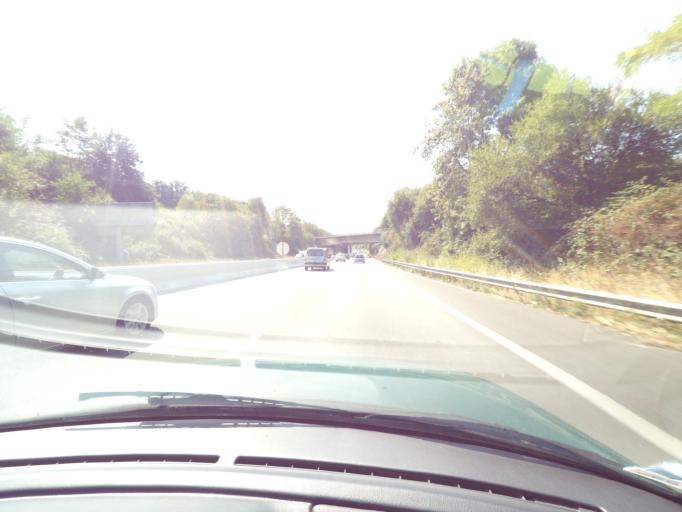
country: FR
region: Limousin
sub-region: Departement de la Haute-Vienne
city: Limoges
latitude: 45.8516
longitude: 1.2760
